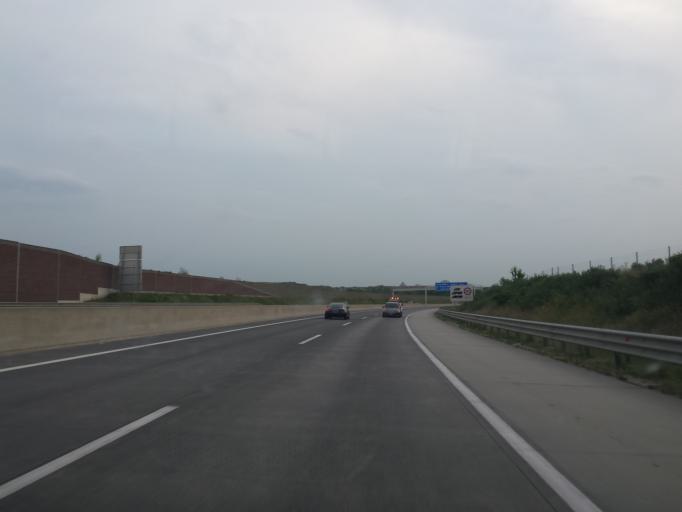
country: AT
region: Lower Austria
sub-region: Politischer Bezirk Ganserndorf
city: Aderklaa
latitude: 48.2675
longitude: 16.4975
